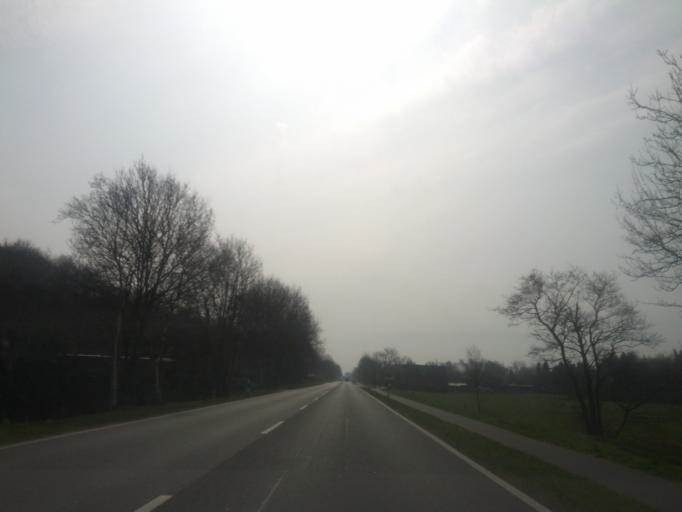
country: DE
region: Lower Saxony
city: Lutetsburg
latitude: 53.5766
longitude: 7.2348
